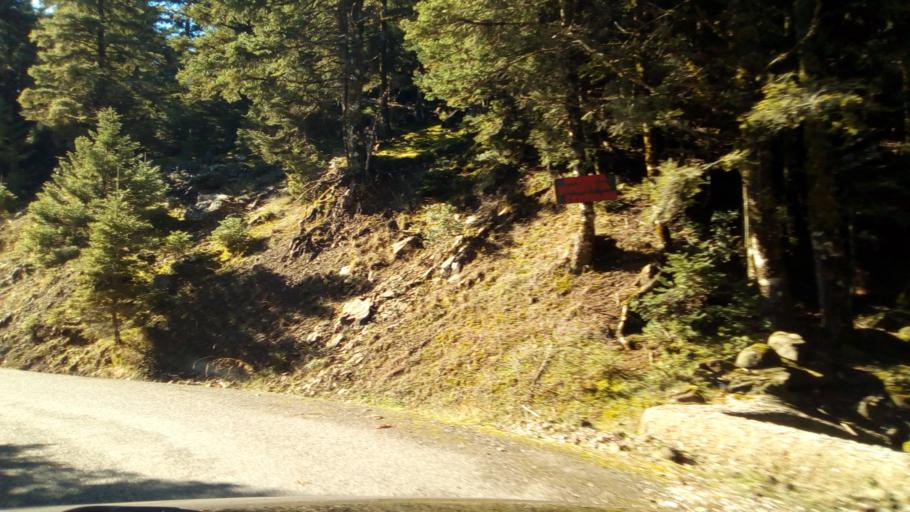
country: GR
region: West Greece
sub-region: Nomos Aitolias kai Akarnanias
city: Nafpaktos
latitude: 38.5380
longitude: 21.8430
